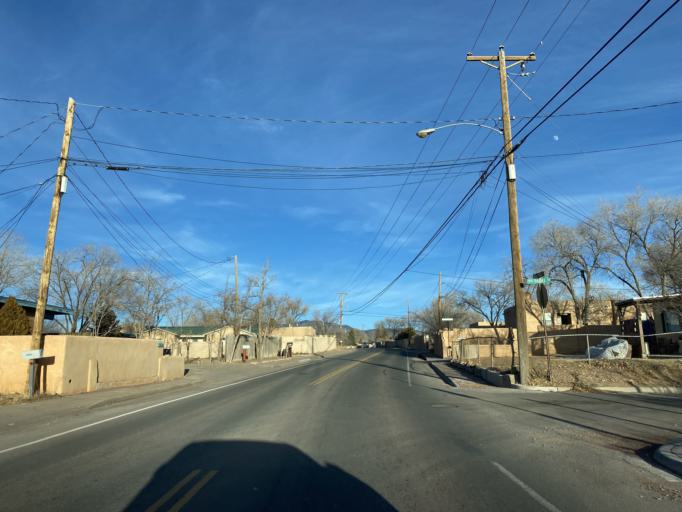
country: US
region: New Mexico
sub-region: Santa Fe County
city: Santa Fe
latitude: 35.6729
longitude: -105.9790
